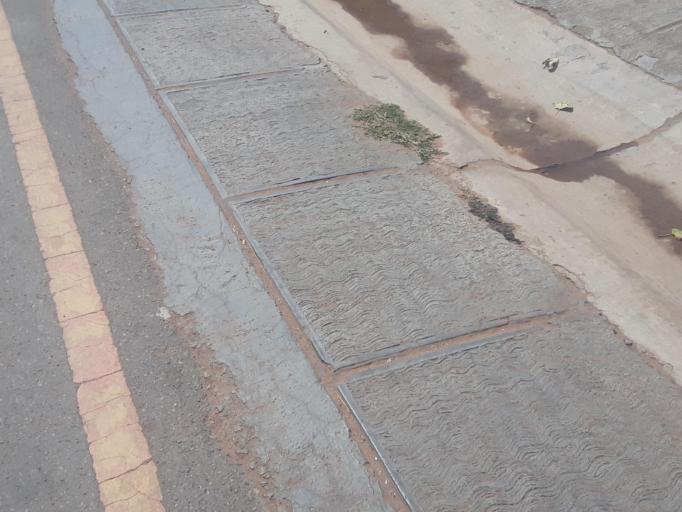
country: ZM
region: Lusaka
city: Lusaka
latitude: -15.3590
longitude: 28.2812
